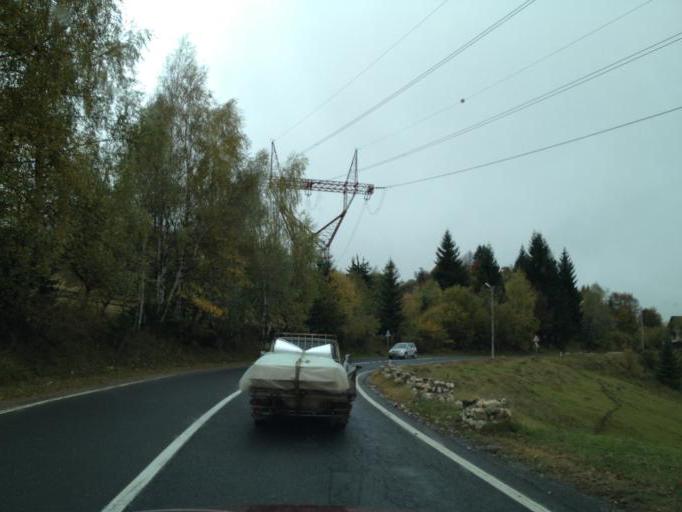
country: RO
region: Brasov
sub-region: Comuna Fundata
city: Fundata
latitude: 45.4579
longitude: 25.2826
